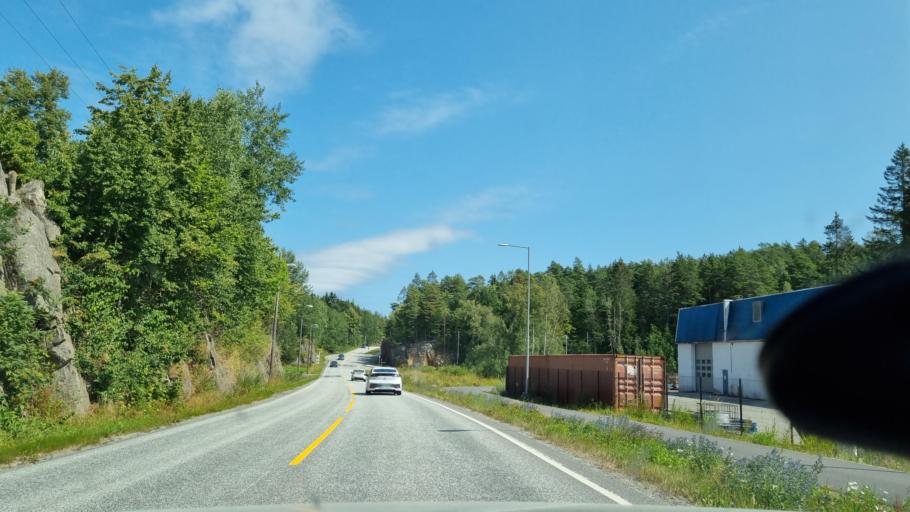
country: NO
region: Aust-Agder
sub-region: Arendal
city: Arendal
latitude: 58.4662
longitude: 8.8368
